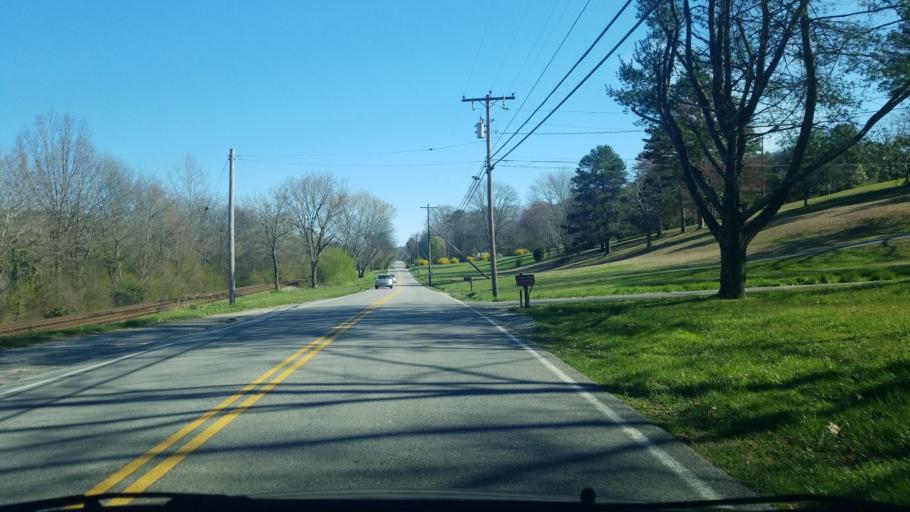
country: US
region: Tennessee
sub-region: Hamilton County
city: Soddy-Daisy
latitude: 35.2265
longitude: -85.1972
